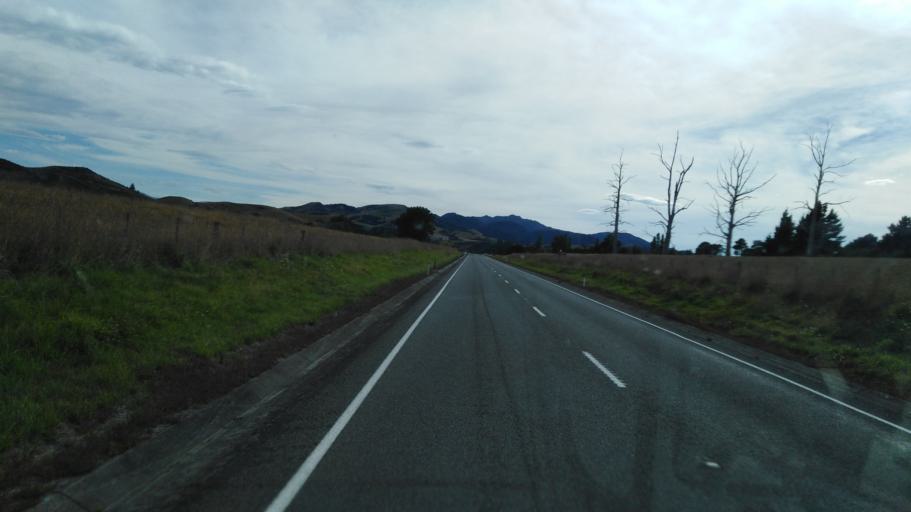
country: NZ
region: Canterbury
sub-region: Kaikoura District
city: Kaikoura
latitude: -42.6452
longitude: 173.3187
